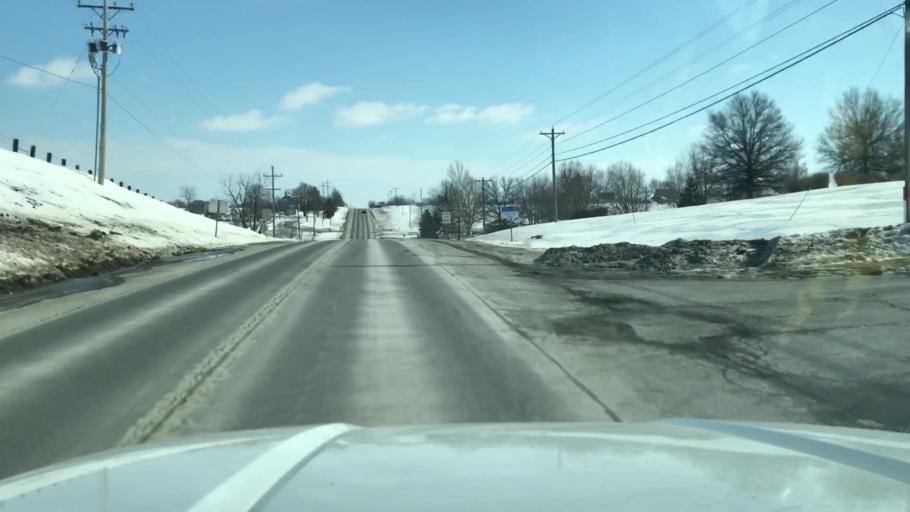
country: US
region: Missouri
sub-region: Nodaway County
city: Maryville
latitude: 40.3446
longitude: -94.8125
